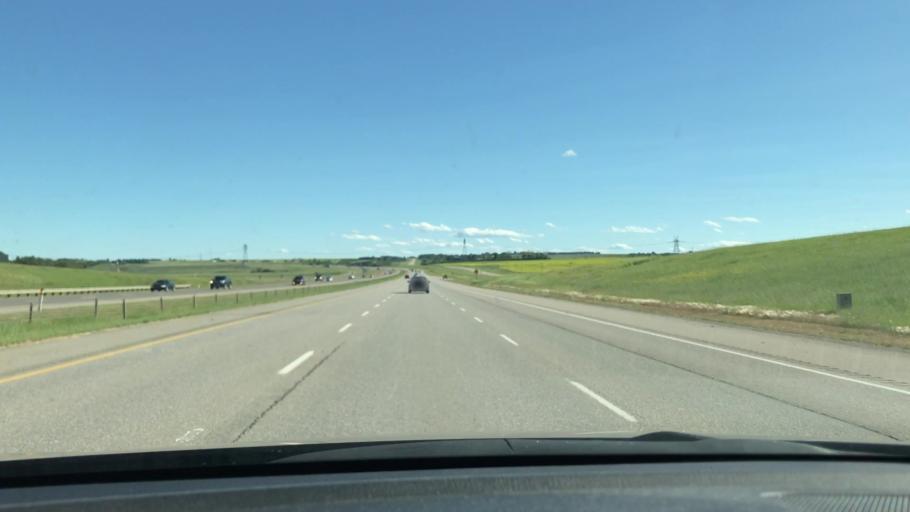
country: CA
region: Alberta
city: Crossfield
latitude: 51.4746
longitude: -114.0253
